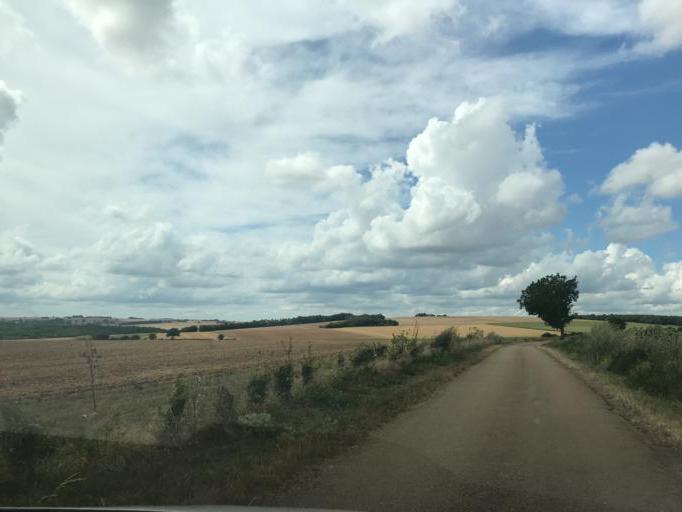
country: FR
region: Bourgogne
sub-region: Departement de l'Yonne
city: Fontenailles
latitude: 47.5785
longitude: 3.3458
